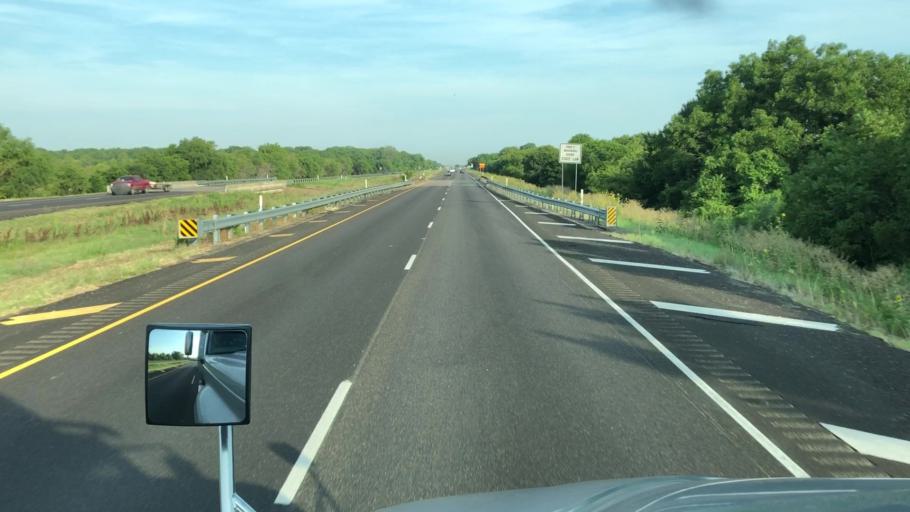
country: US
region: Texas
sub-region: McLennan County
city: Bellmead
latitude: 31.5384
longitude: -97.0396
